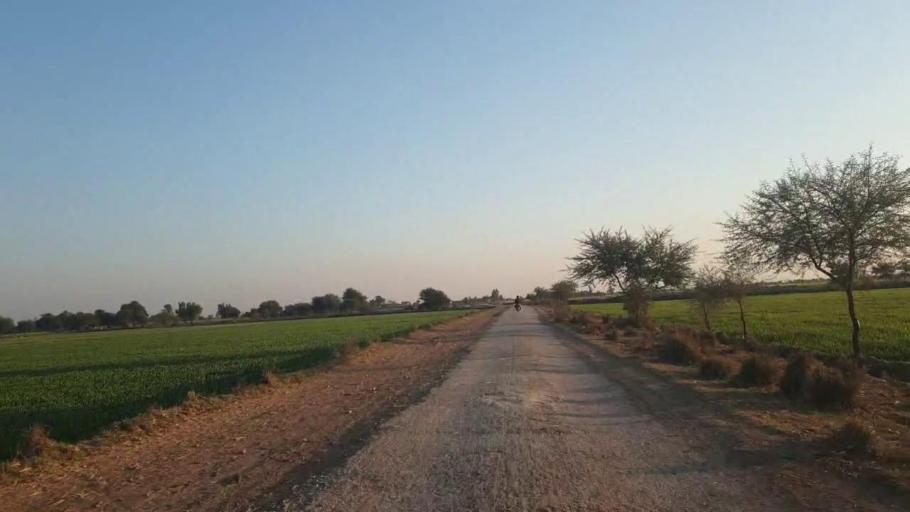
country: PK
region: Sindh
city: Khadro
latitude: 26.0800
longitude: 68.6988
